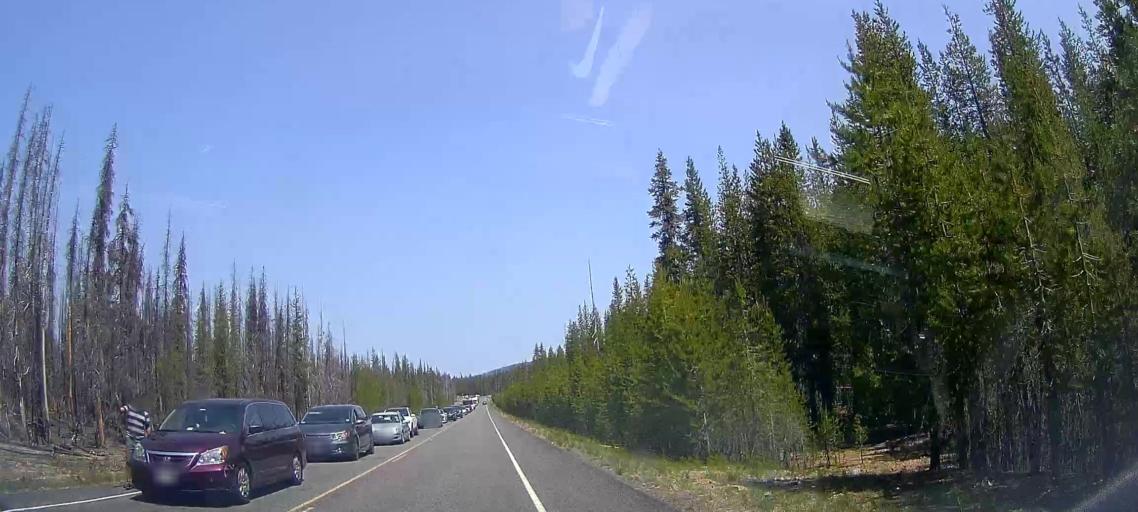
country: US
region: Oregon
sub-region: Lane County
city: Oakridge
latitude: 43.0818
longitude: -122.1172
